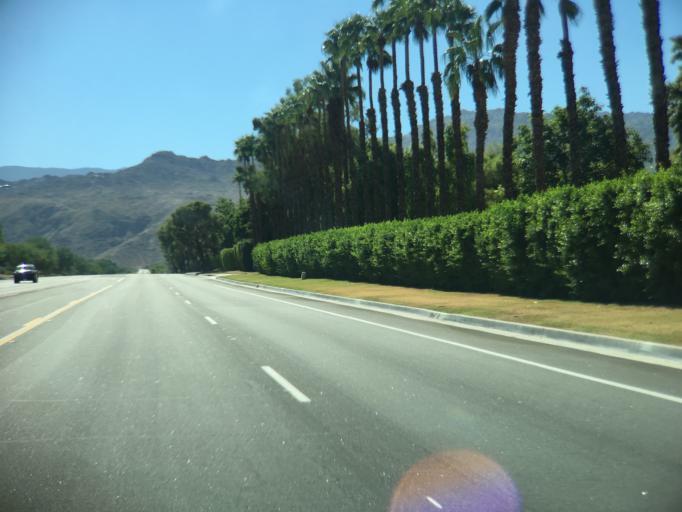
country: US
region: California
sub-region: Riverside County
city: Palm Desert
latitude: 33.6938
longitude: -116.4009
